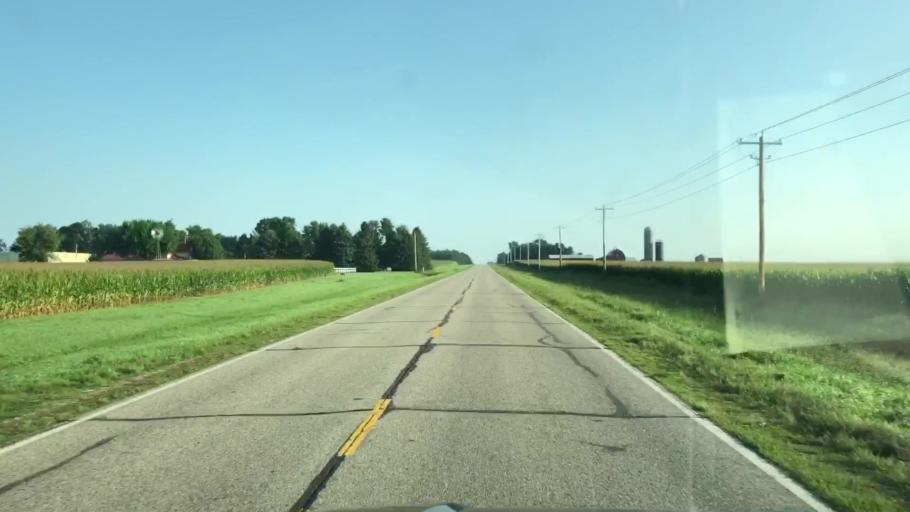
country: US
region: Iowa
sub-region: Lyon County
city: George
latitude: 43.3674
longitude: -95.9983
